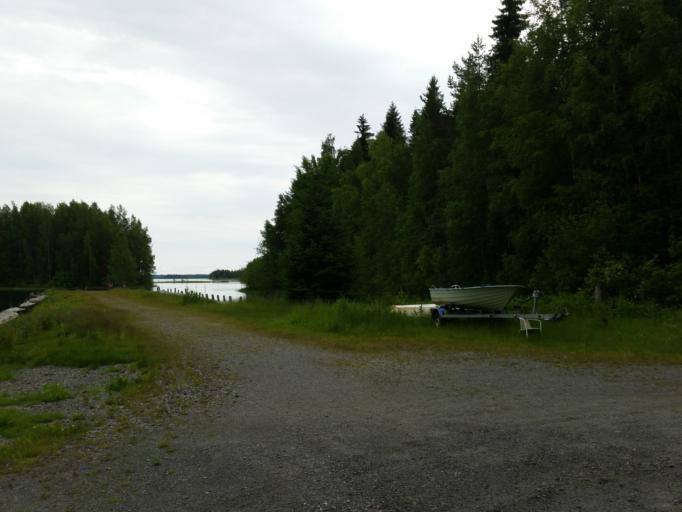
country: FI
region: Northern Savo
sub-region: Sisae-Savo
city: Tervo
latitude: 63.0056
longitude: 26.6896
